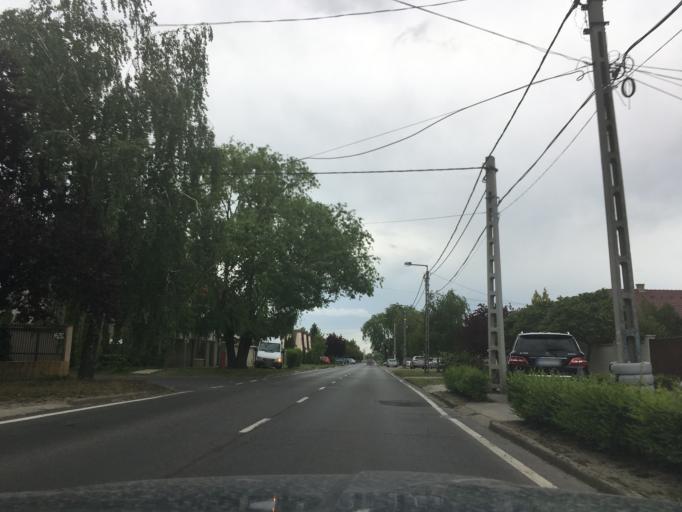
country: HU
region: Hajdu-Bihar
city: Debrecen
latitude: 47.5364
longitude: 21.6713
